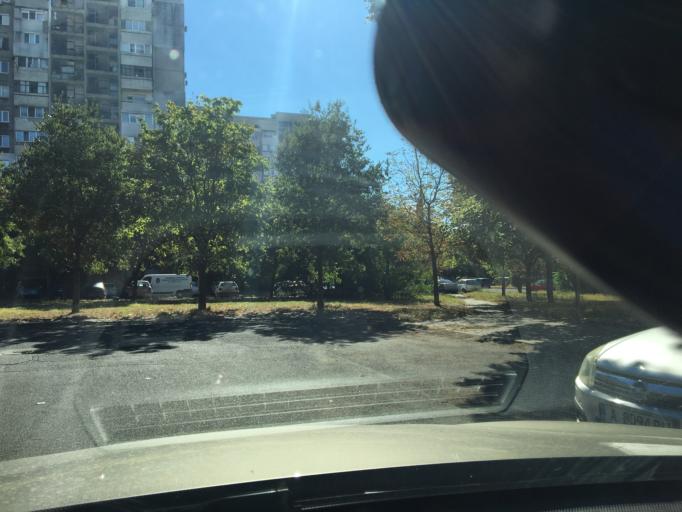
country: BG
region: Burgas
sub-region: Obshtina Burgas
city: Burgas
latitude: 42.5159
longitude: 27.4519
